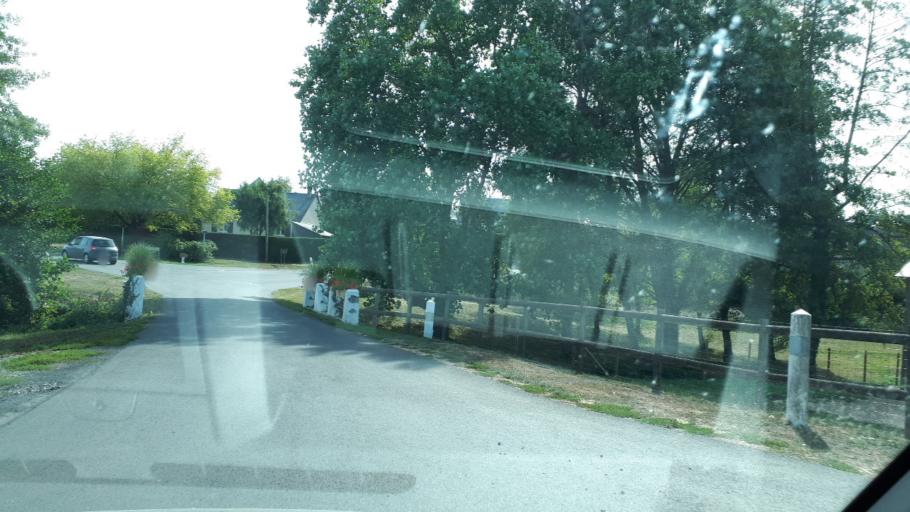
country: FR
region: Centre
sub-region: Departement du Loir-et-Cher
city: Montoire-sur-le-Loir
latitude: 47.7256
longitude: 0.8300
